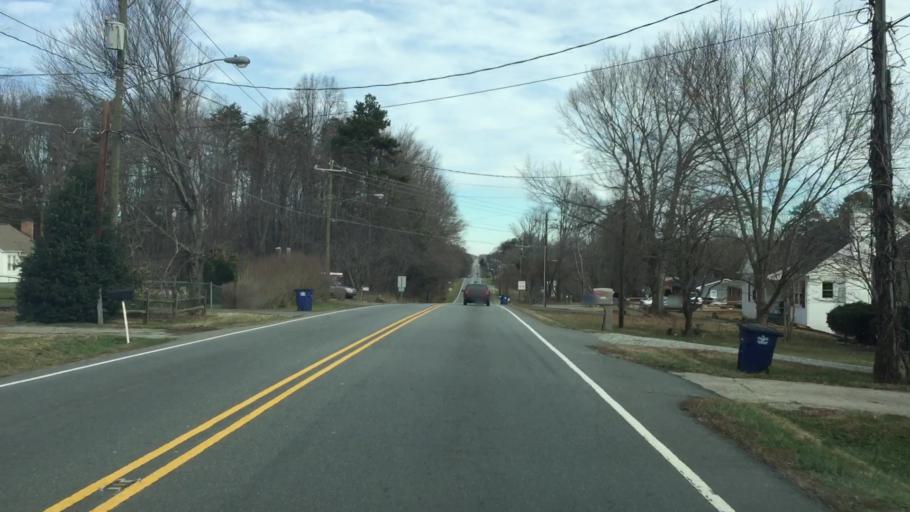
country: US
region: North Carolina
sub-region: Forsyth County
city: Walkertown
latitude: 36.1278
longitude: -80.1747
